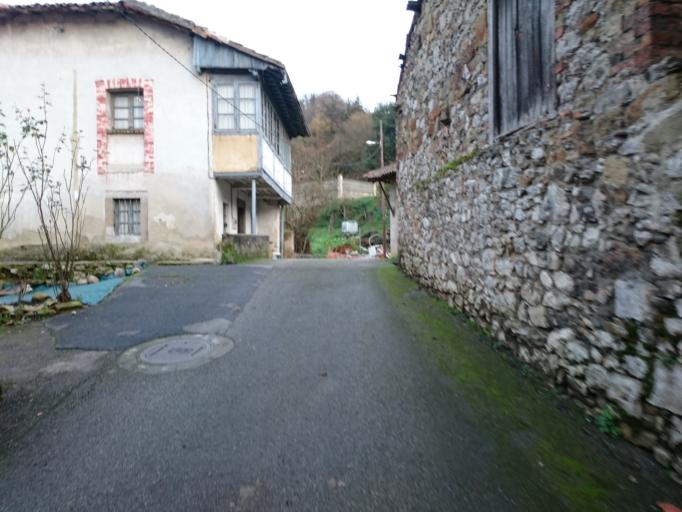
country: ES
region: Asturias
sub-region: Province of Asturias
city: Oviedo
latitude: 43.3194
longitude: -5.8005
